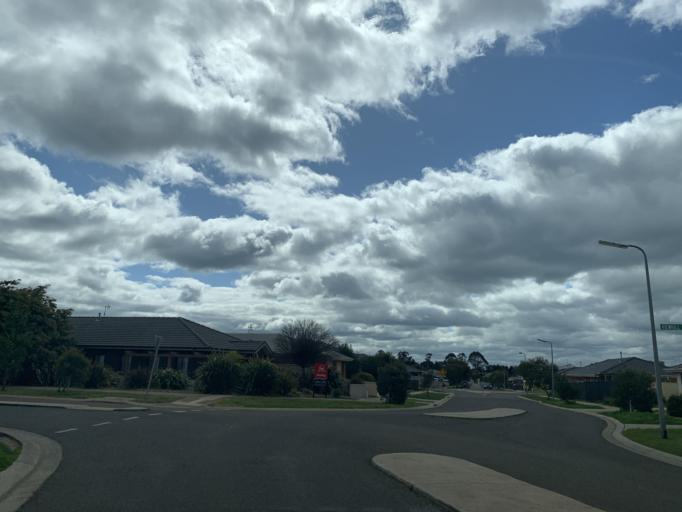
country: AU
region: Victoria
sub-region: Whittlesea
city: Whittlesea
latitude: -37.2913
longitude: 144.9356
